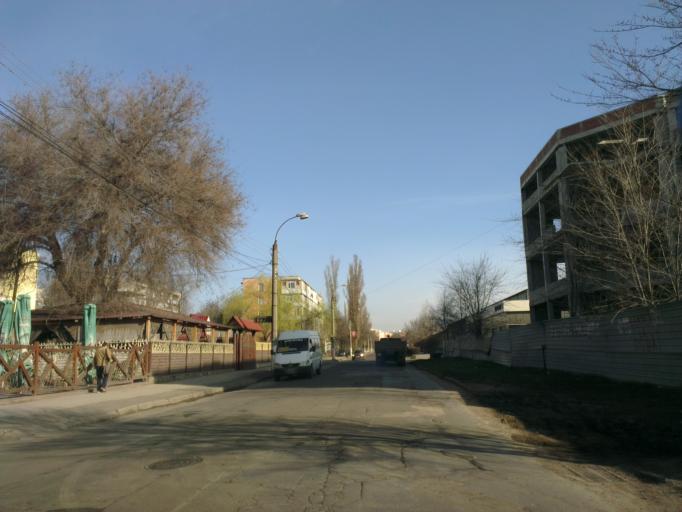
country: MD
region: Chisinau
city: Chisinau
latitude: 47.0208
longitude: 28.8830
